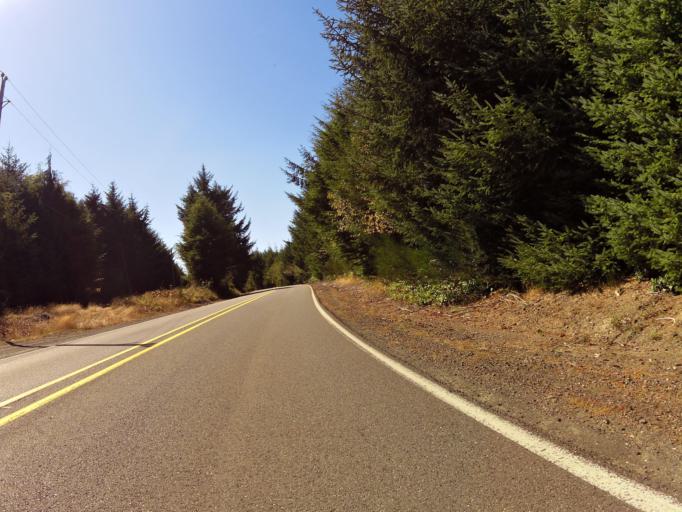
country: US
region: Oregon
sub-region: Coos County
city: Barview
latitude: 43.2807
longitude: -124.3446
